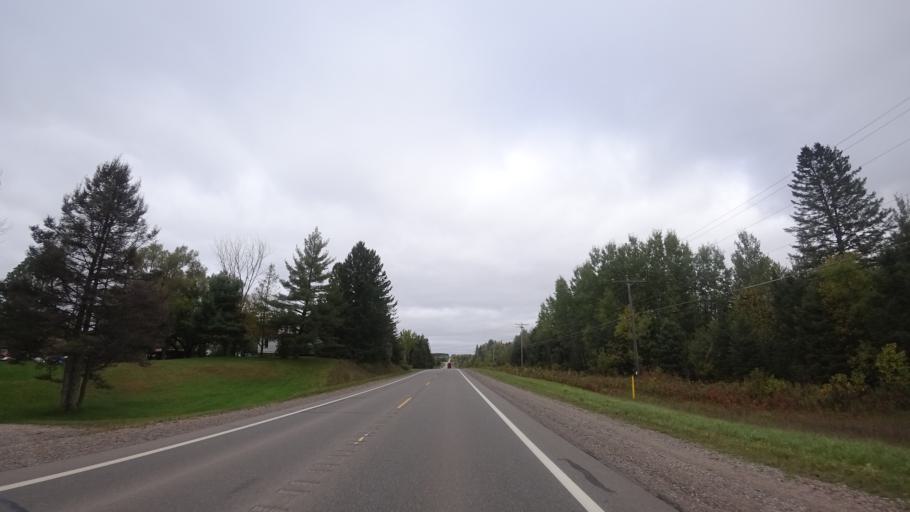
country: US
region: Wisconsin
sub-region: Florence County
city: Florence
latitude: 46.0984
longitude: -88.0757
